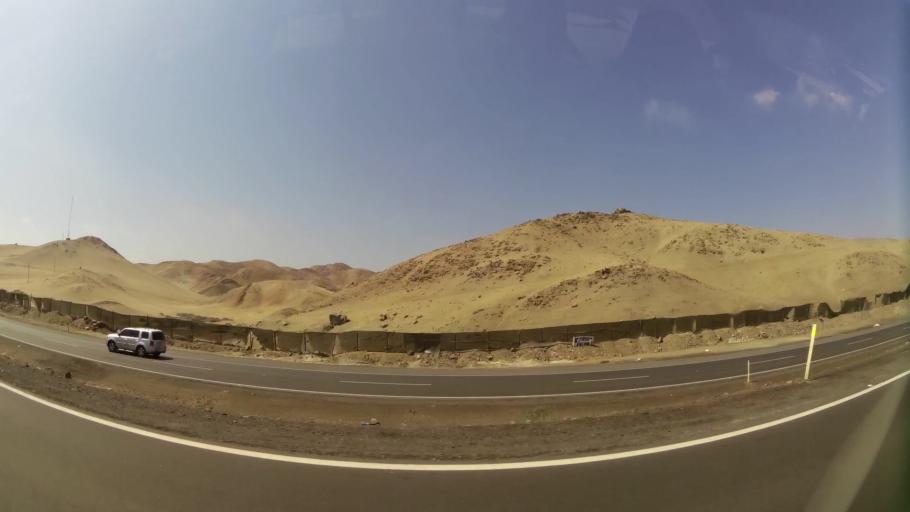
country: PE
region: Lima
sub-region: Provincia de Canete
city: Quilmana
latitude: -12.9549
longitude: -76.5009
